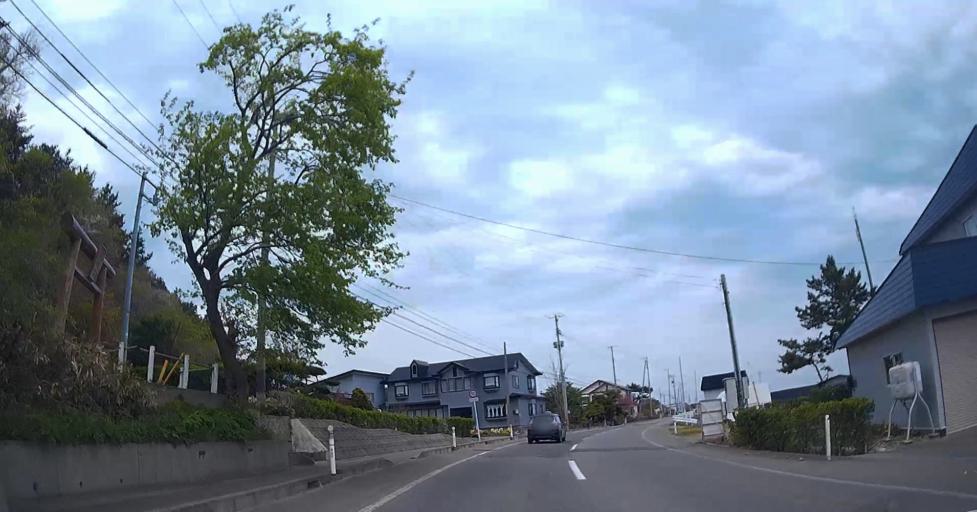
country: JP
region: Aomori
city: Shimokizukuri
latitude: 40.9978
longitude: 140.3467
